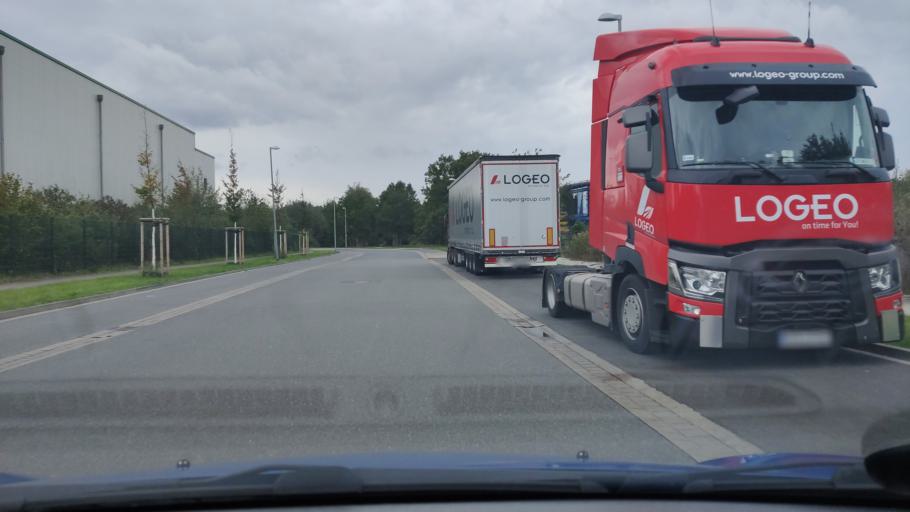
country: DE
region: Lower Saxony
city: Garbsen-Mitte
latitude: 52.4310
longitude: 9.6599
